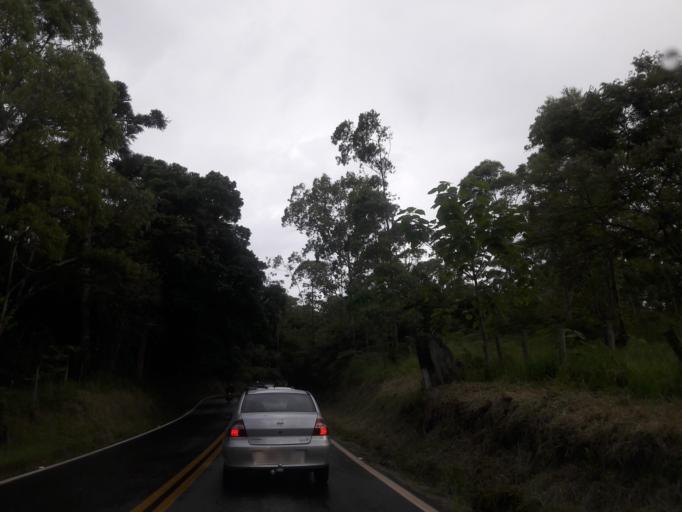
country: BR
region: Sao Paulo
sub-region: Aruja
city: Aruja
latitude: -23.3308
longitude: -46.4335
